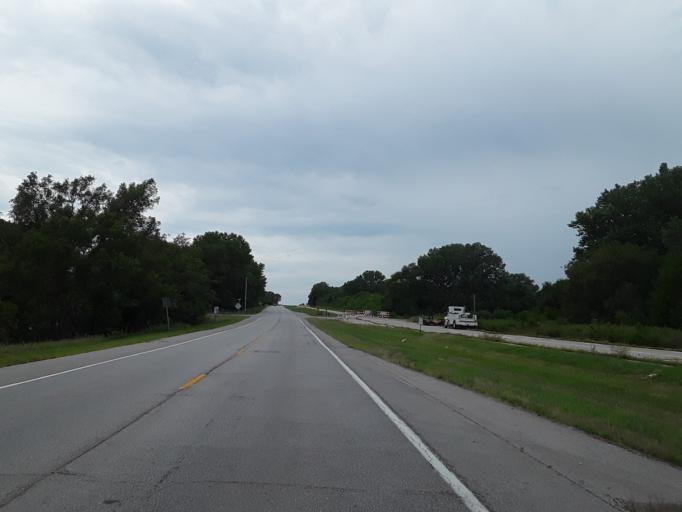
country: US
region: Nebraska
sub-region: Douglas County
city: Bennington
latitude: 41.3650
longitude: -96.0598
